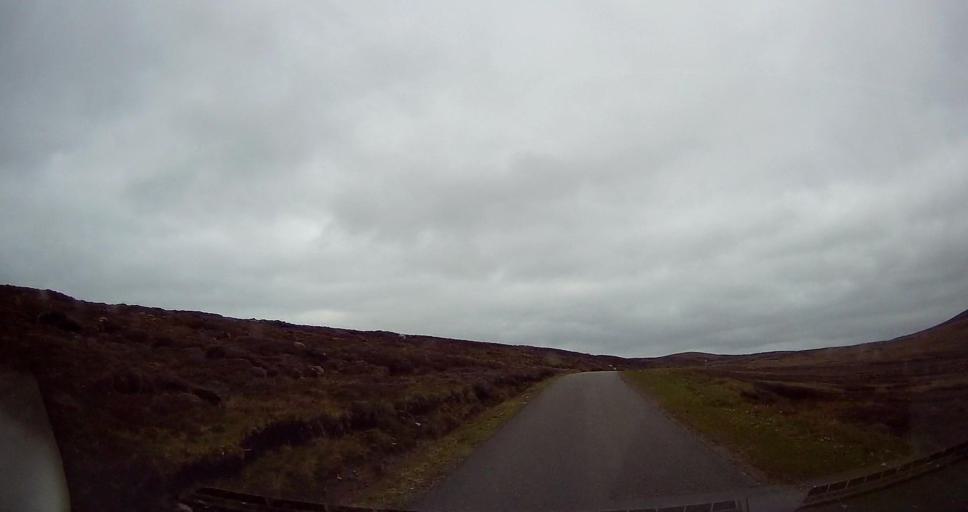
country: GB
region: Scotland
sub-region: Shetland Islands
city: Lerwick
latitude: 60.3130
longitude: -1.3418
